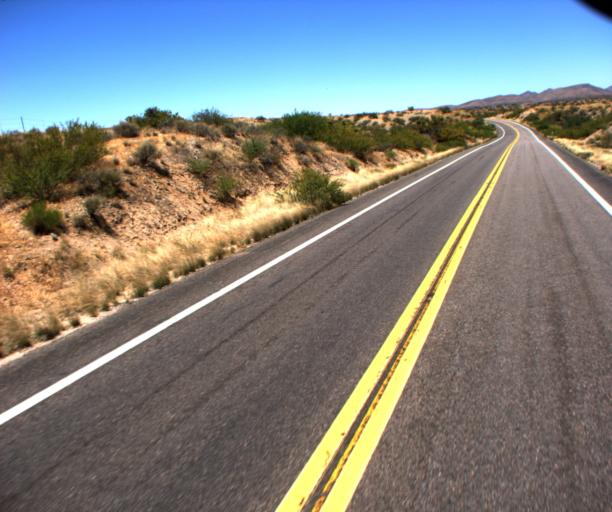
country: US
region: Arizona
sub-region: Gila County
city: Globe
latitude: 33.3464
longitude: -110.7305
